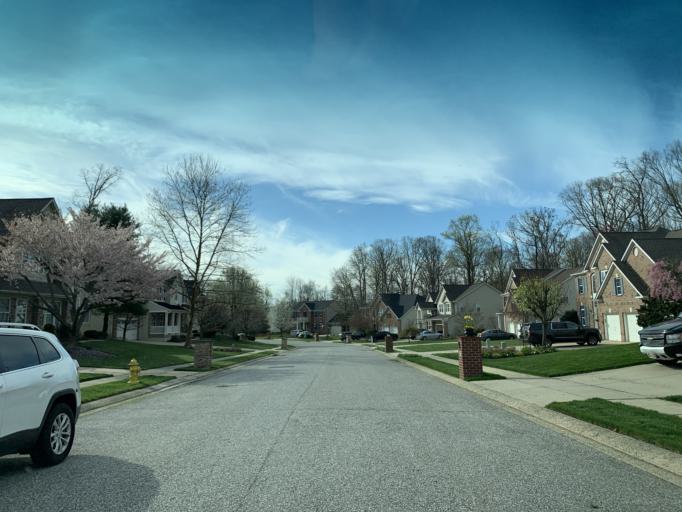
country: US
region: Maryland
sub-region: Harford County
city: North Bel Air
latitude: 39.5669
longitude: -76.3362
